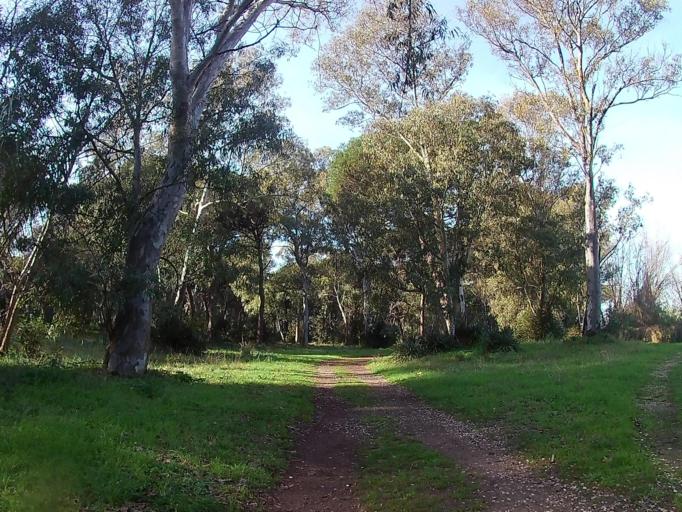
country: IT
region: Latium
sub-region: Citta metropolitana di Roma Capitale
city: Lido di Ostia
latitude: 41.7458
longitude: 12.2805
